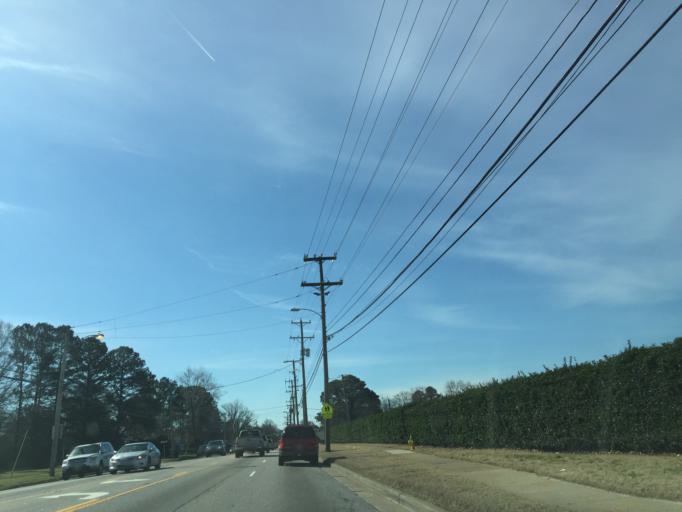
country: US
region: Virginia
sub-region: City of Norfolk
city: Norfolk
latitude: 36.8896
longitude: -76.2592
